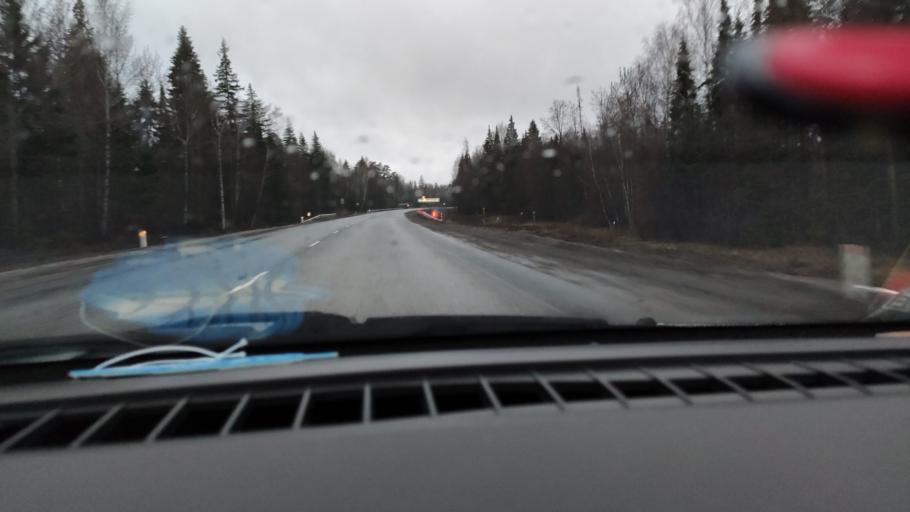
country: RU
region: Udmurtiya
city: Alnashi
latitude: 56.0906
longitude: 52.4442
